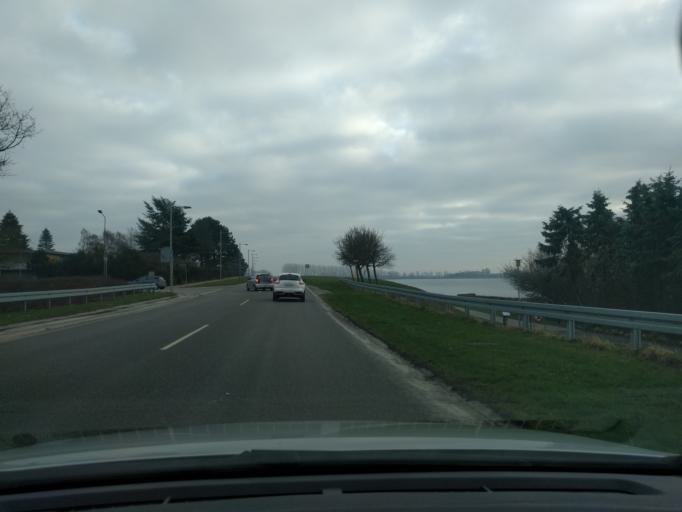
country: DK
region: Zealand
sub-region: Guldborgsund Kommune
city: Nykobing Falster
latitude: 54.7541
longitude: 11.8771
